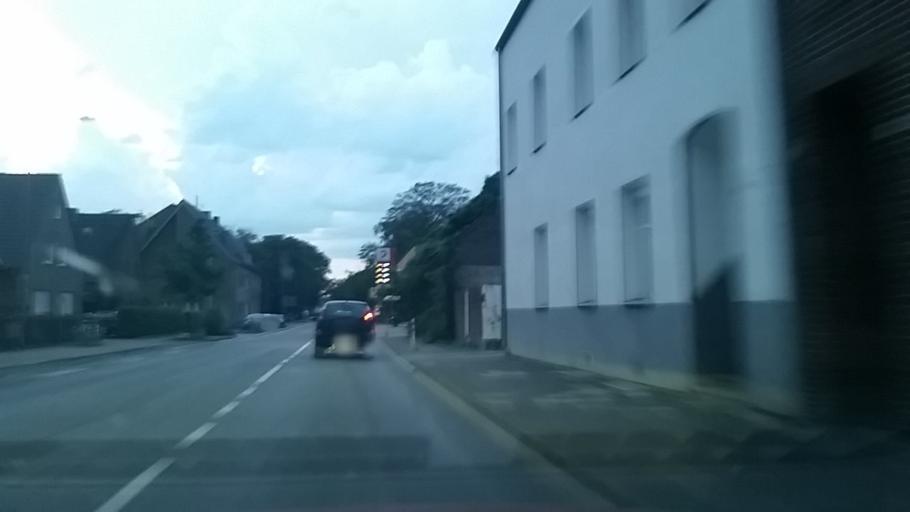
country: DE
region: North Rhine-Westphalia
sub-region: Regierungsbezirk Dusseldorf
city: Willich
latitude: 51.2666
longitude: 6.5523
